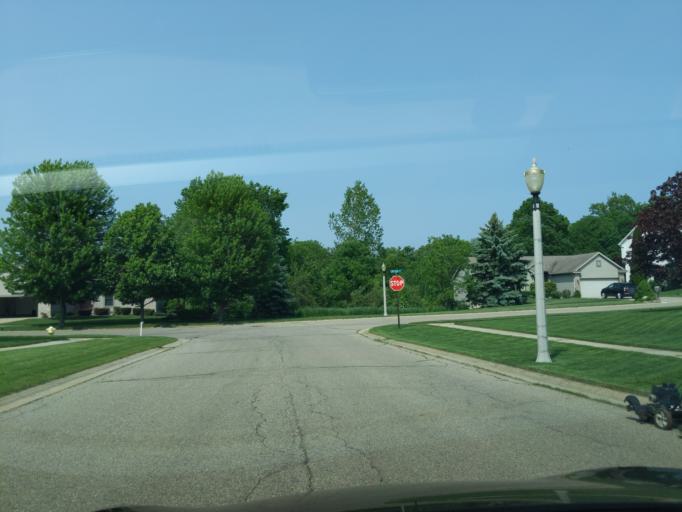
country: US
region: Michigan
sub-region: Eaton County
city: Waverly
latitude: 42.7502
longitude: -84.6550
